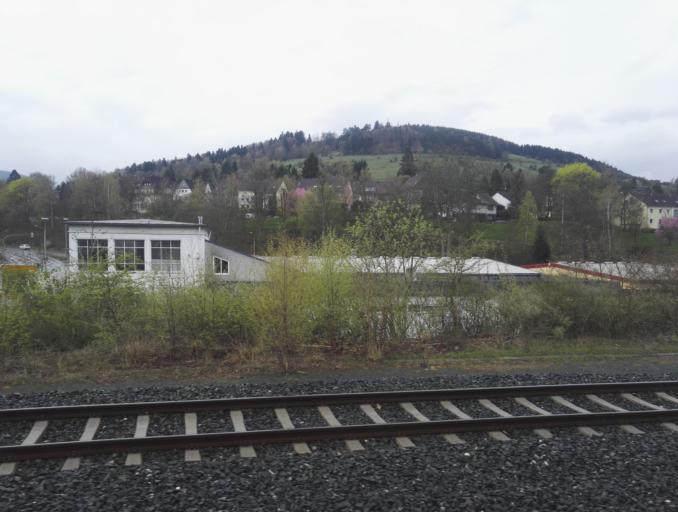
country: DE
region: Lower Saxony
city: Goslar
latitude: 51.9131
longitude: 10.4171
